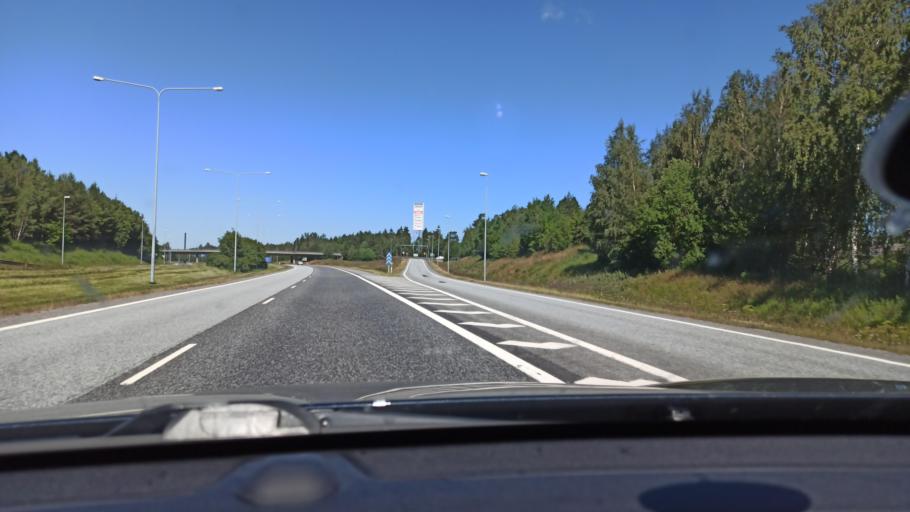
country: FI
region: Ostrobothnia
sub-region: Vaasa
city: Teeriniemi
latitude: 63.0680
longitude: 21.7014
